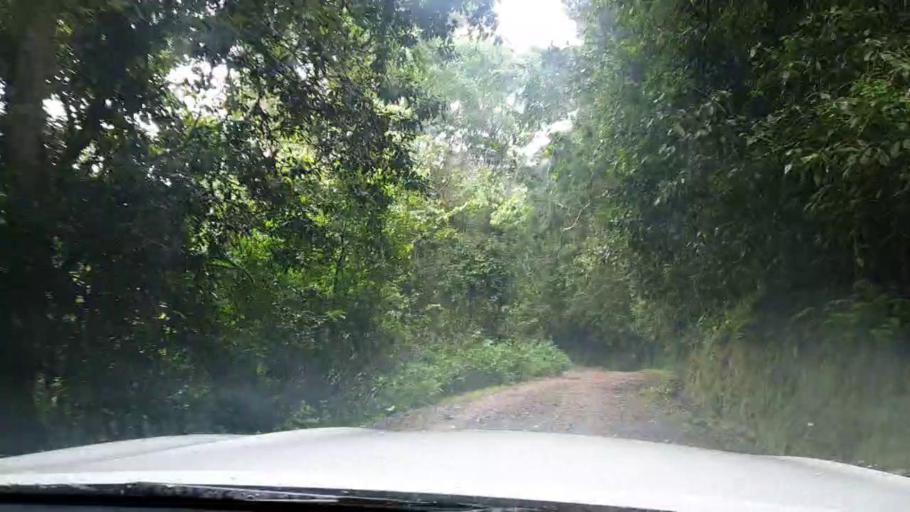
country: RW
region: Western Province
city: Cyangugu
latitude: -2.5570
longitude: 28.9791
